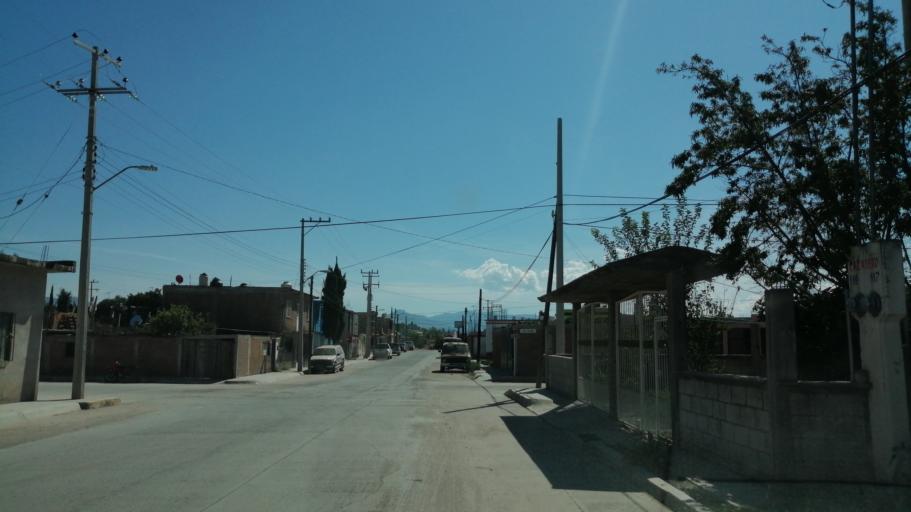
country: MX
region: Durango
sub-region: Santiago Papasquiaro
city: Santiago Papasquiaro
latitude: 25.0493
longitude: -105.4365
